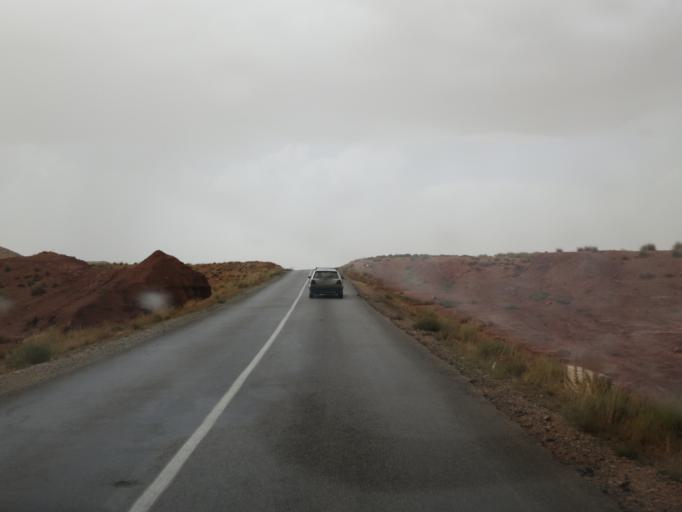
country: MA
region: Meknes-Tafilalet
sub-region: Khenifra
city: Itzer
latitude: 32.8569
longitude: -4.9464
